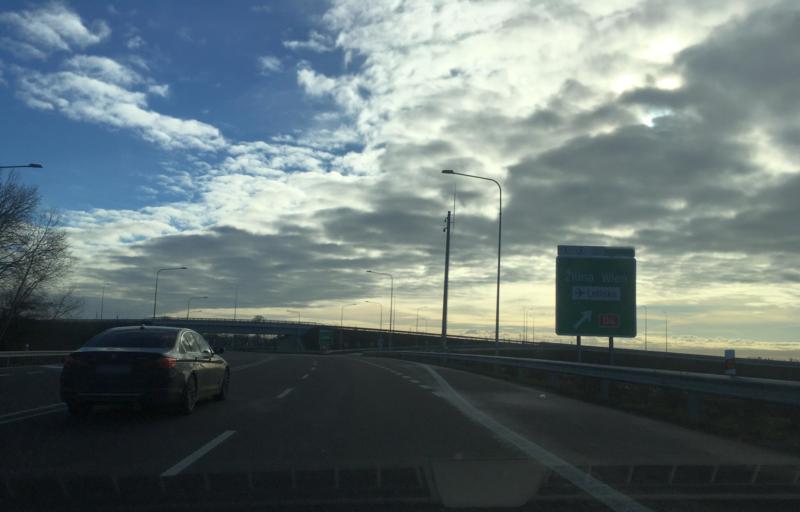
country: AT
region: Burgenland
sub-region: Politischer Bezirk Neusiedl am See
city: Deutsch Jahrndorf
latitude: 48.0761
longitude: 17.1324
